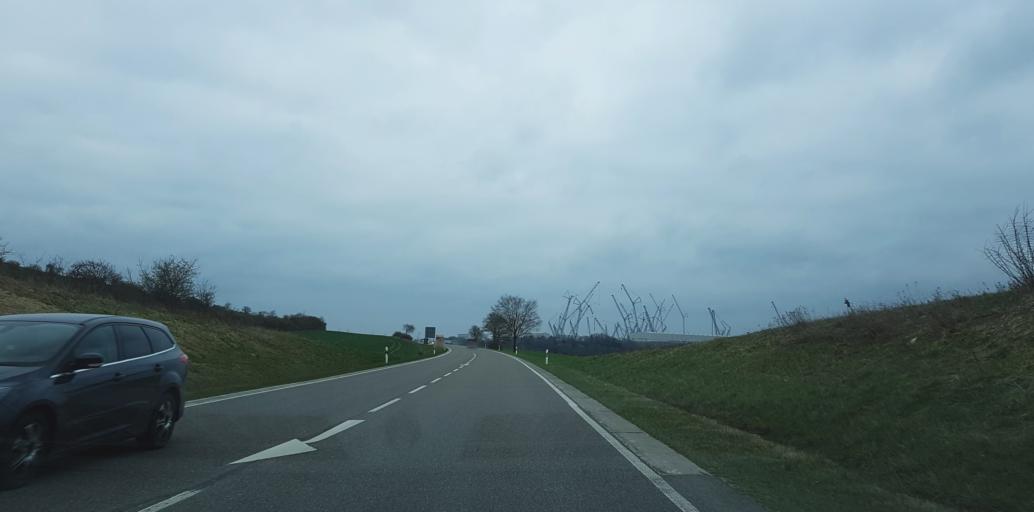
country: DE
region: Baden-Wuerttemberg
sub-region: Tuebingen Region
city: Allmendingen
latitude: 48.3142
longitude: 9.7241
